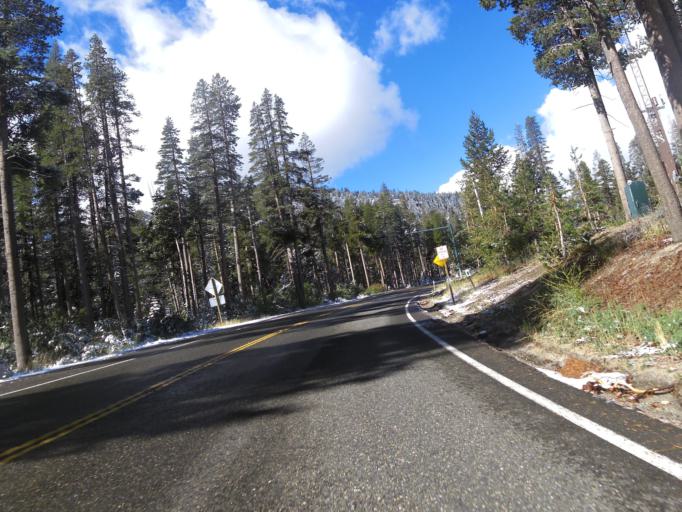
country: US
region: California
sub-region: El Dorado County
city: South Lake Tahoe
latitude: 38.8131
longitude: -120.0296
